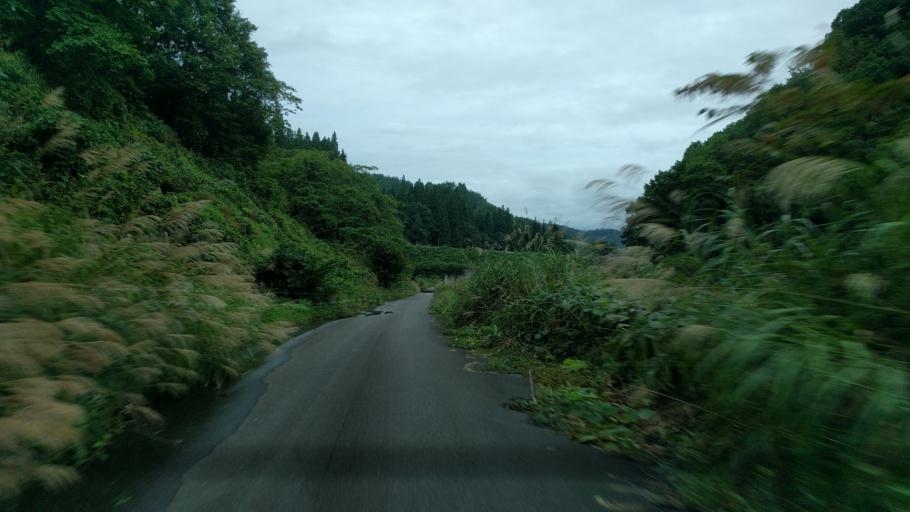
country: JP
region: Fukushima
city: Kitakata
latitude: 37.4691
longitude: 139.7729
